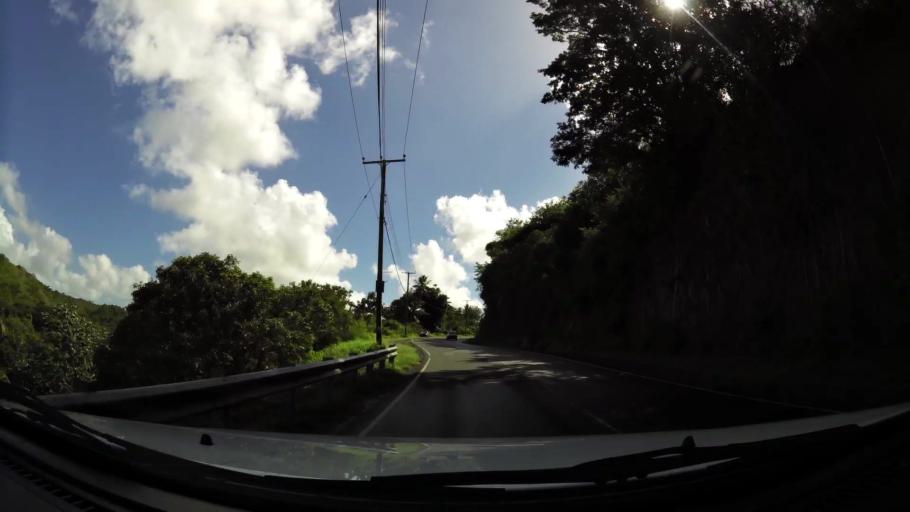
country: LC
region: Choiseul Quarter
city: Choiseul
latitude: 13.7720
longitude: -61.0477
